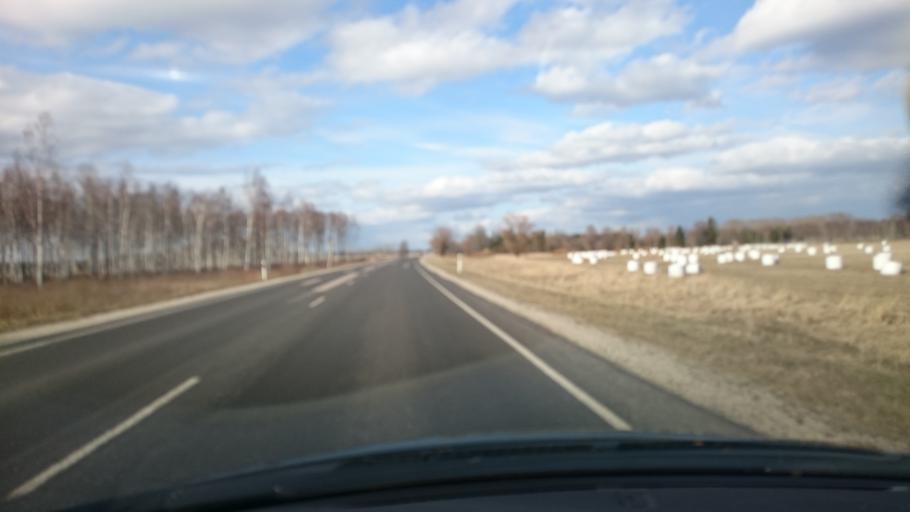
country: EE
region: Harju
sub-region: Nissi vald
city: Turba
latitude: 58.8549
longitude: 24.0706
